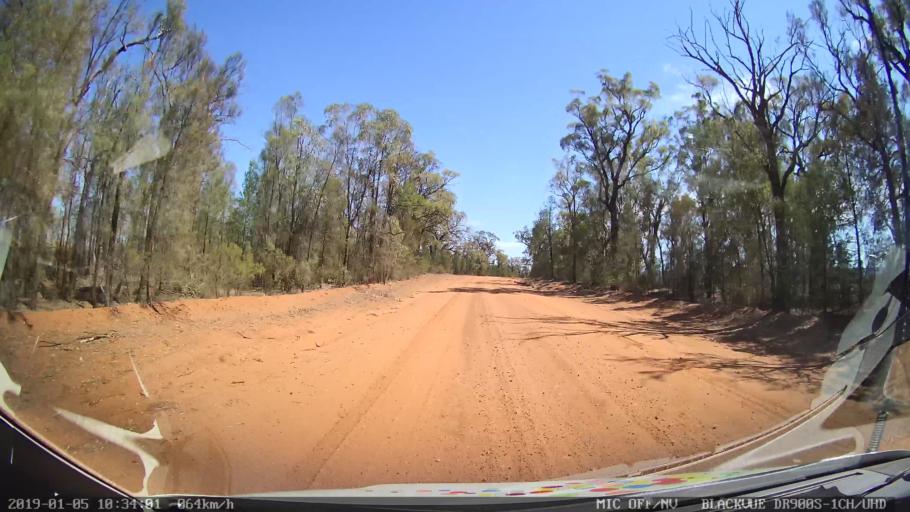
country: AU
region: New South Wales
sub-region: Gilgandra
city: Gilgandra
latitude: -31.5020
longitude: 148.9292
